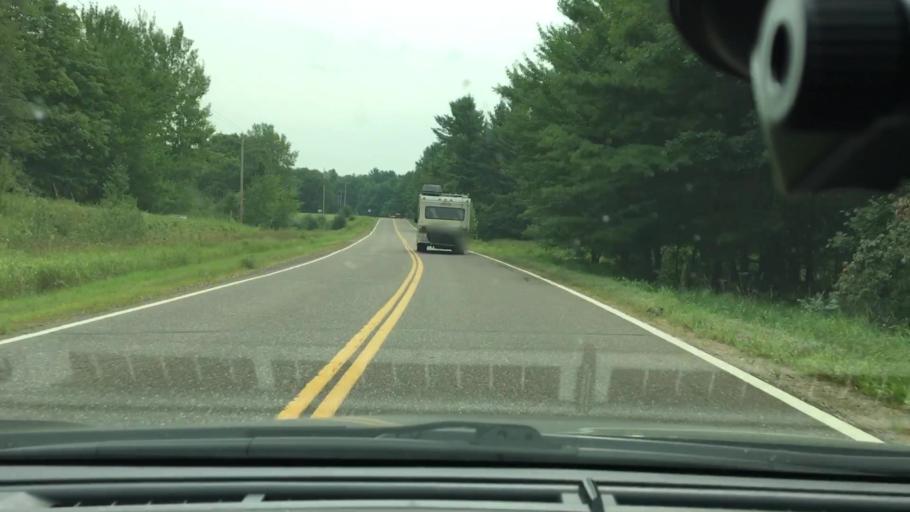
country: US
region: Minnesota
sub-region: Aitkin County
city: Aitkin
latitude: 46.4040
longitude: -93.8055
